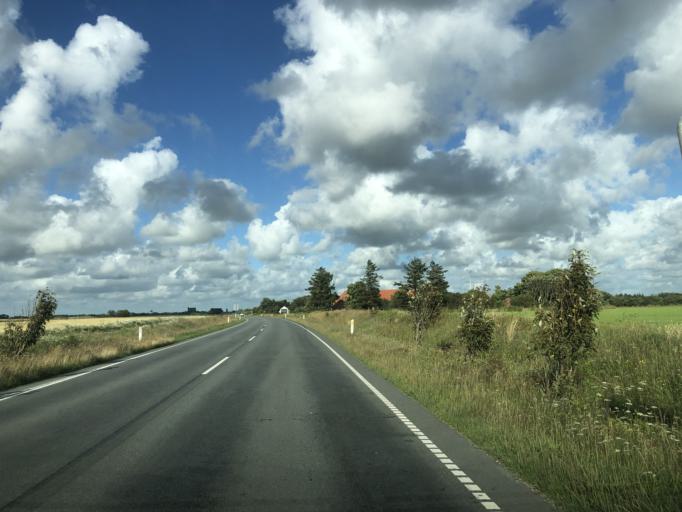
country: DK
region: Central Jutland
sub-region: Lemvig Kommune
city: Lemvig
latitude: 56.5036
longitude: 8.2762
